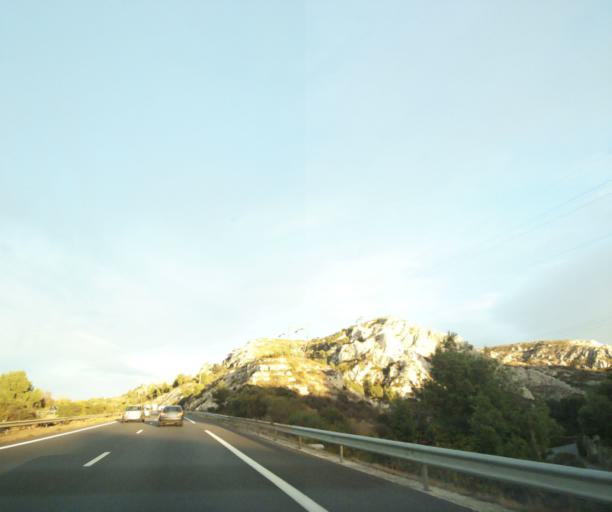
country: FR
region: Provence-Alpes-Cote d'Azur
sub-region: Departement des Bouches-du-Rhone
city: Le Rove
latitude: 43.3921
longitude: 5.2751
